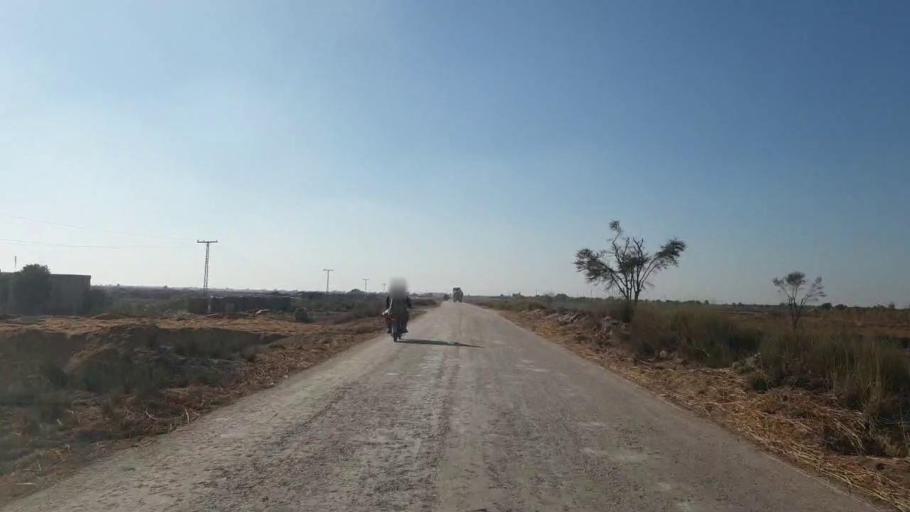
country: PK
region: Sindh
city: New Badah
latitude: 27.3250
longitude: 68.0535
